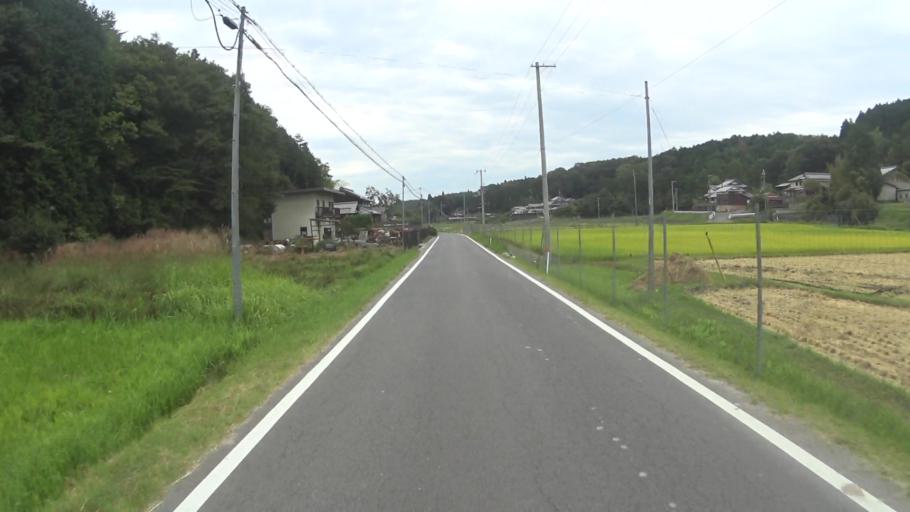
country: JP
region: Mie
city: Ueno-ebisumachi
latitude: 34.8454
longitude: 136.0094
